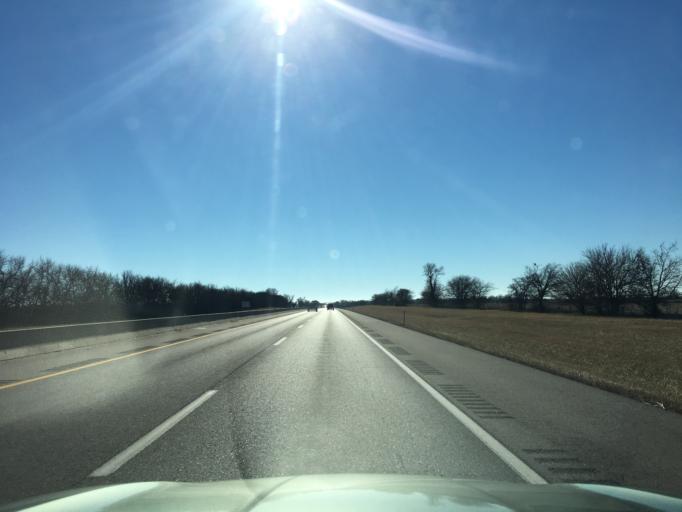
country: US
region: Kansas
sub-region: Sumner County
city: Wellington
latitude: 37.0994
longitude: -97.3387
